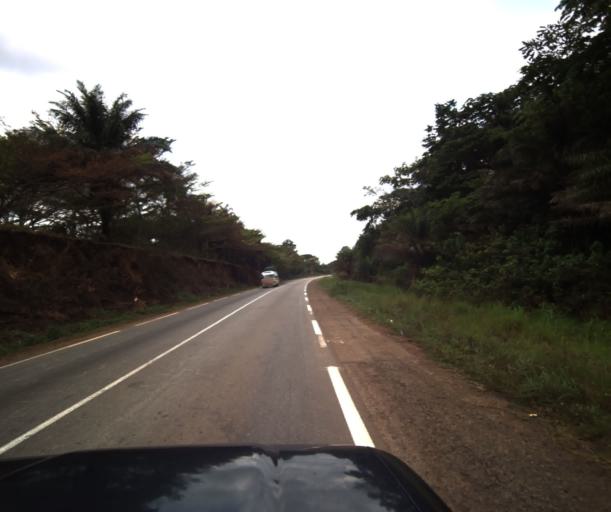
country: CM
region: Centre
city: Eseka
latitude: 3.8349
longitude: 10.9896
